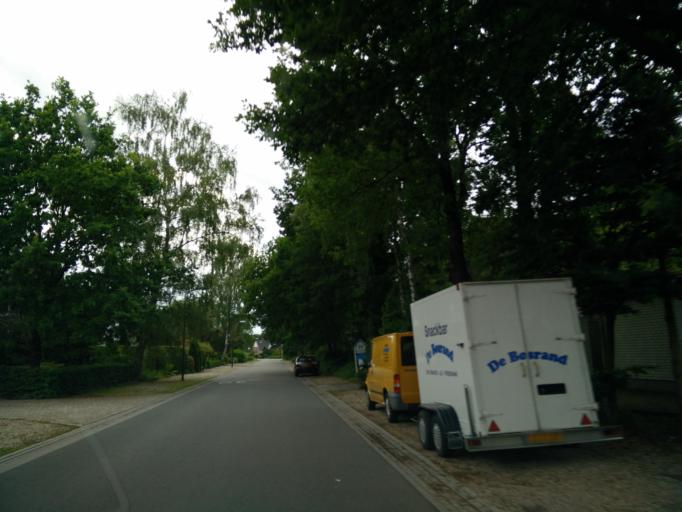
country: NL
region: Gelderland
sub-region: Gemeente Apeldoorn
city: Beekbergen
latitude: 52.1842
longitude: 5.9260
